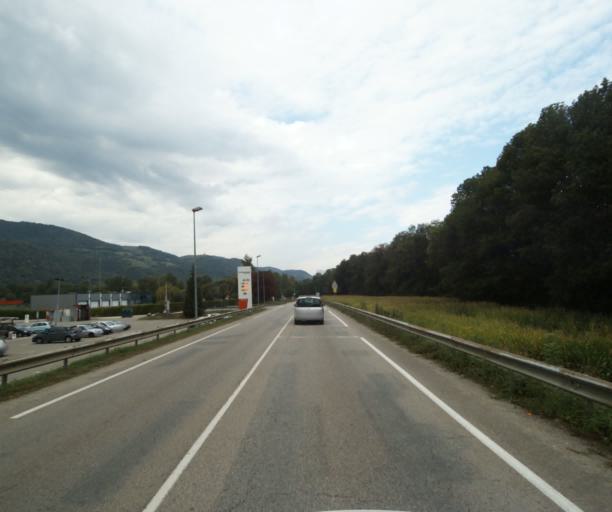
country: FR
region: Rhone-Alpes
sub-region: Departement de l'Isere
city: Domene
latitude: 45.2075
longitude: 5.8279
